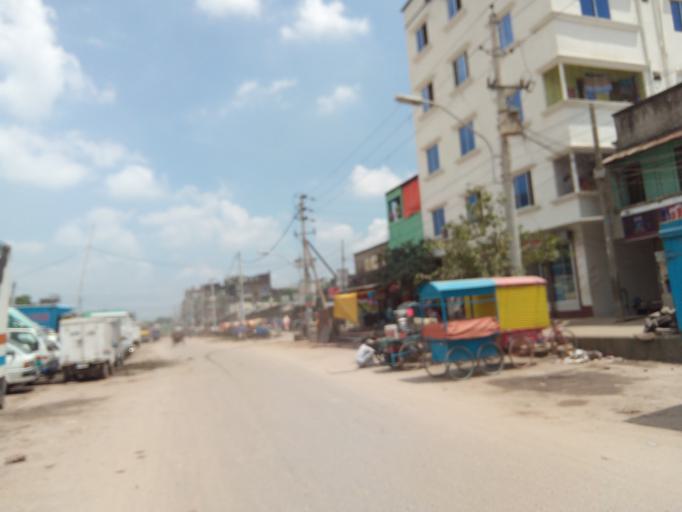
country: BD
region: Dhaka
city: Tungi
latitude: 23.8203
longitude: 90.3779
